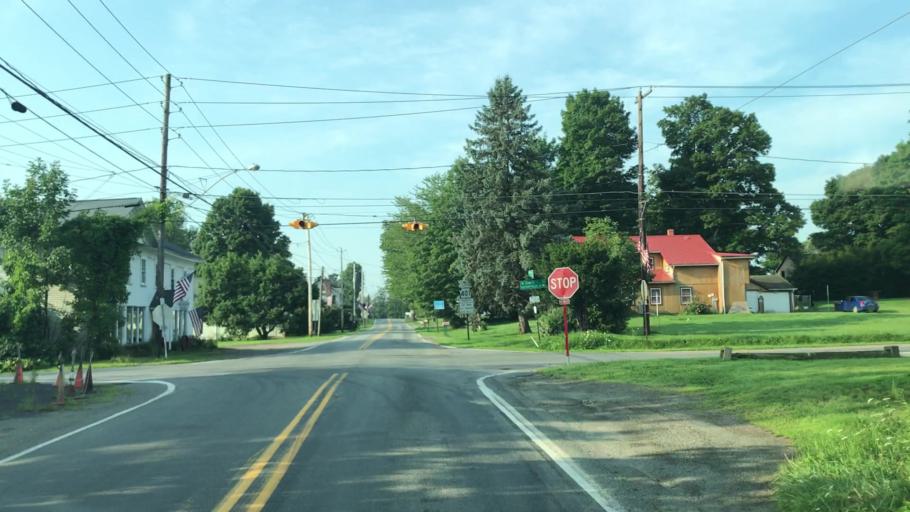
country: US
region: Pennsylvania
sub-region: Lackawanna County
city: Dalton
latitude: 41.5984
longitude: -75.7151
